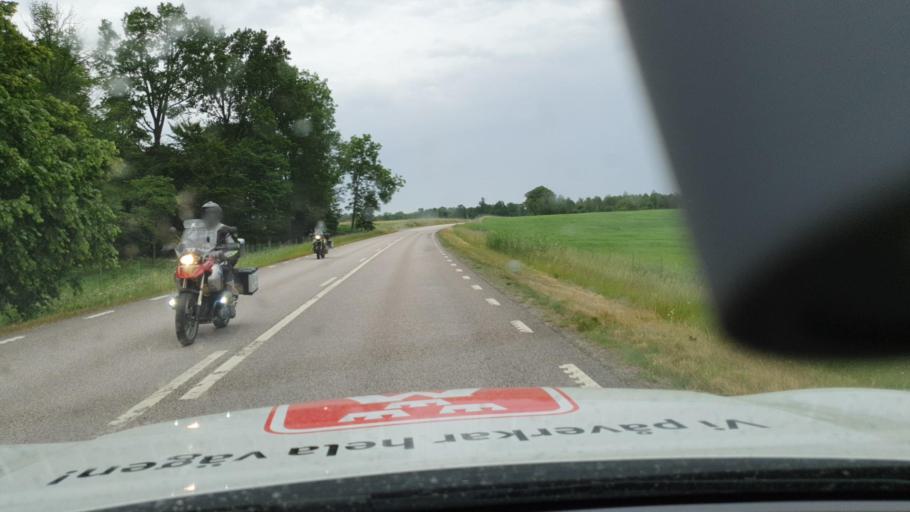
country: SE
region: Vaestra Goetaland
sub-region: Hjo Kommun
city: Hjo
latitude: 58.3408
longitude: 14.3388
